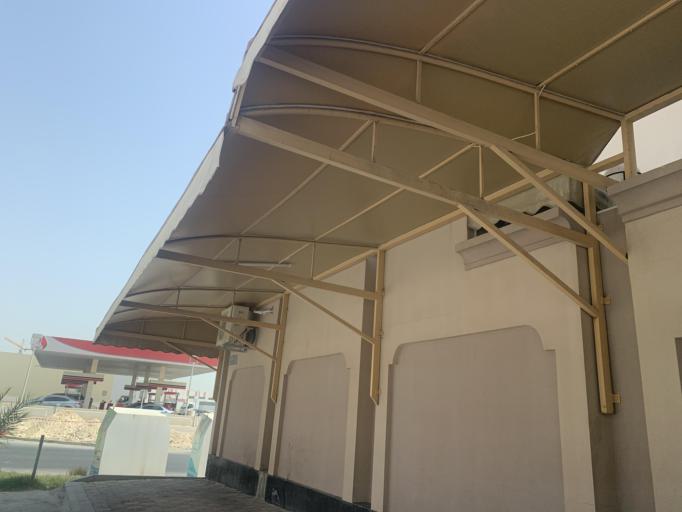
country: BH
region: Northern
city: Madinat `Isa
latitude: 26.1517
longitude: 50.5278
